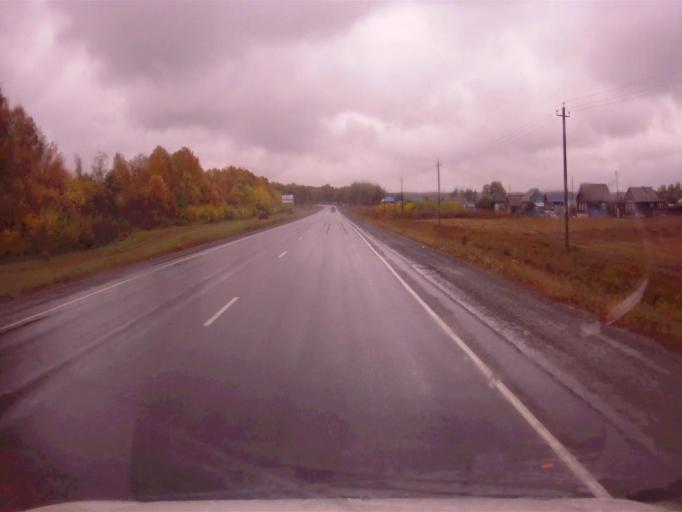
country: RU
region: Chelyabinsk
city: Argayash
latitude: 55.4075
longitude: 61.0557
